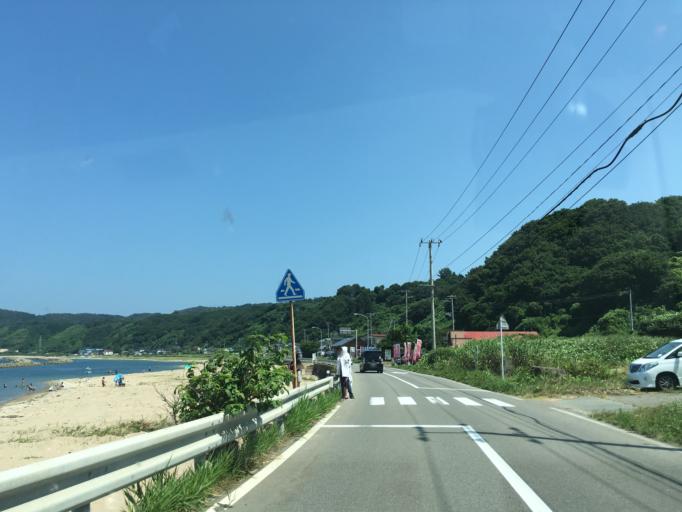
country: JP
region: Akita
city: Tenno
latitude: 39.9459
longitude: 139.7192
